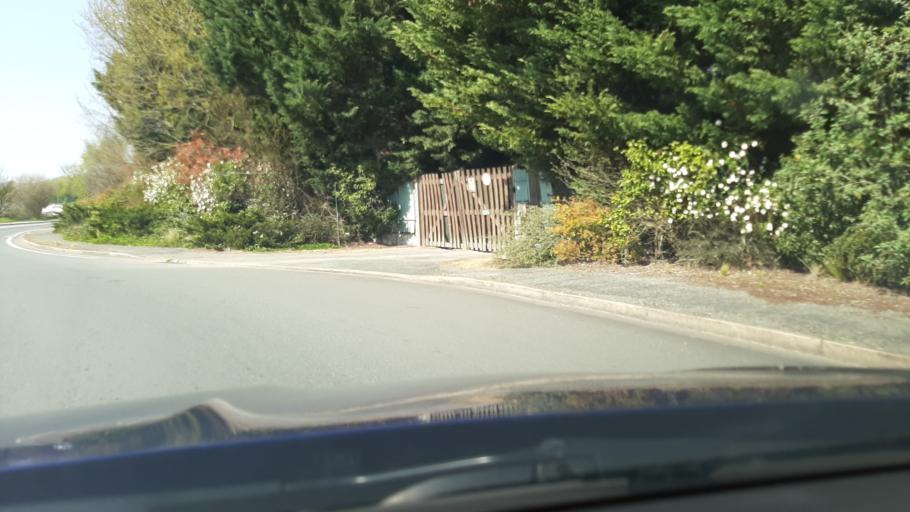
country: FR
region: Pays de la Loire
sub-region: Departement de Maine-et-Loire
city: Trelaze
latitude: 47.4813
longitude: -0.4881
